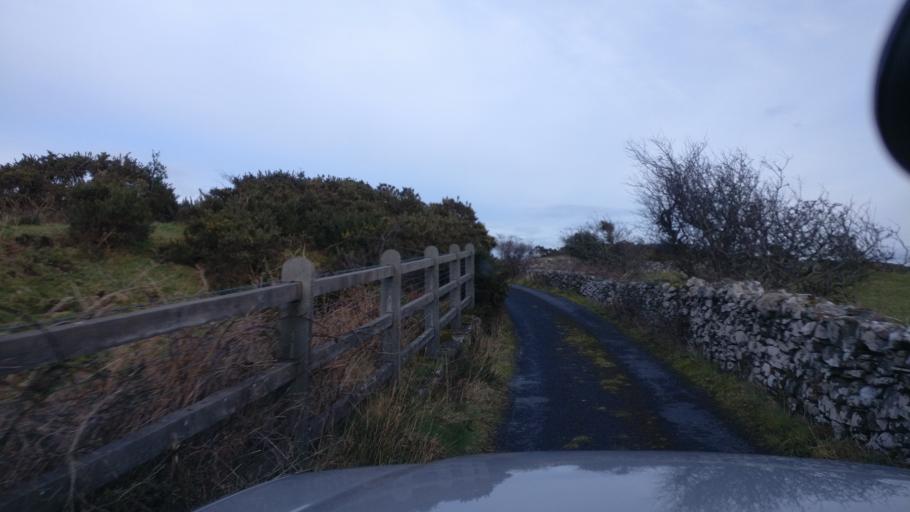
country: IE
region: Connaught
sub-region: County Galway
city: Oughterard
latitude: 53.5238
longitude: -9.3877
